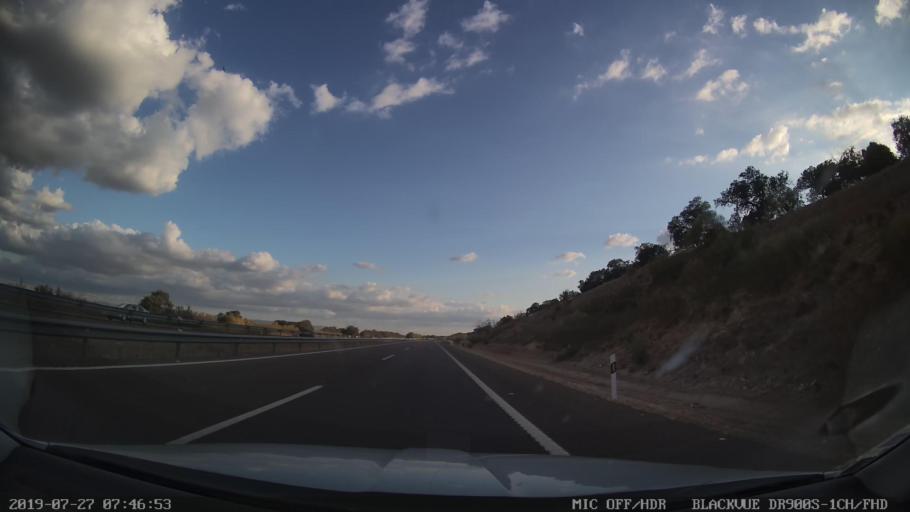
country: ES
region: Extremadura
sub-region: Provincia de Badajoz
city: San Pedro de Merida
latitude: 38.9601
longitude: -6.1586
